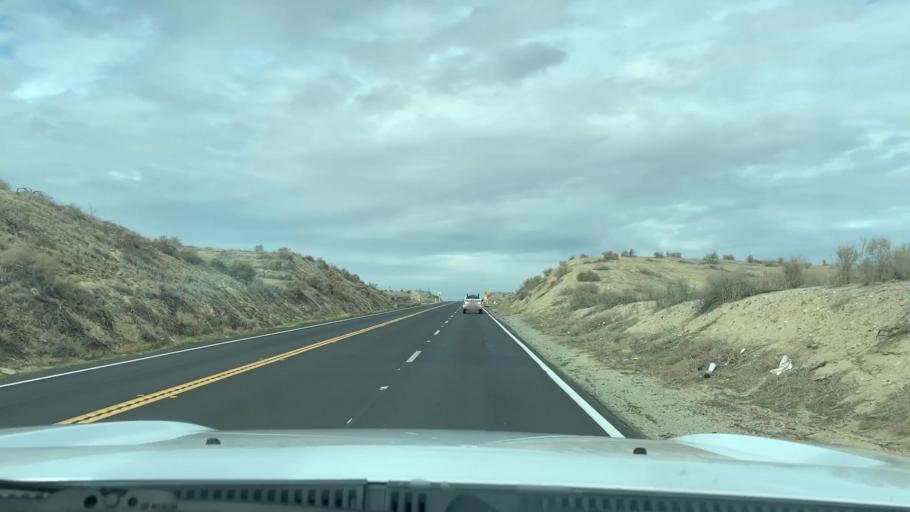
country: US
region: California
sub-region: Kern County
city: Maricopa
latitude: 35.1020
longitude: -119.4167
